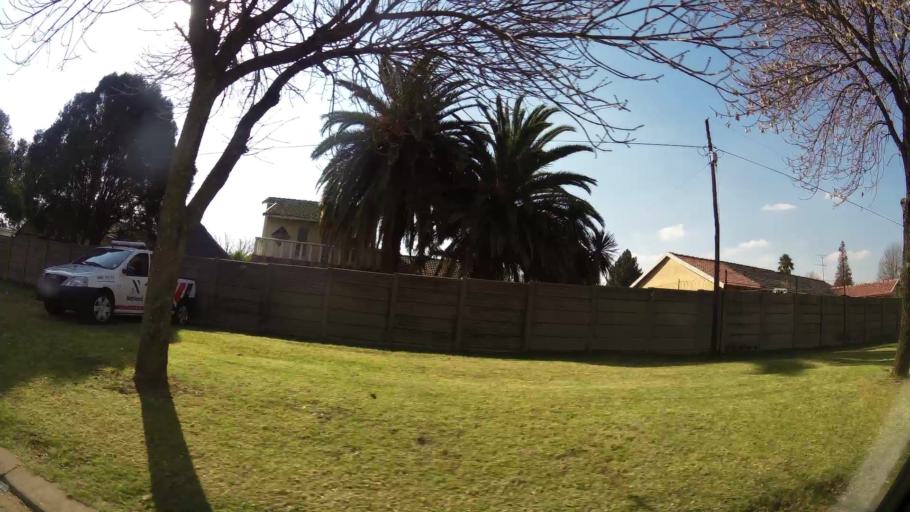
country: ZA
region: Gauteng
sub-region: Ekurhuleni Metropolitan Municipality
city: Benoni
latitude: -26.2416
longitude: 28.3160
